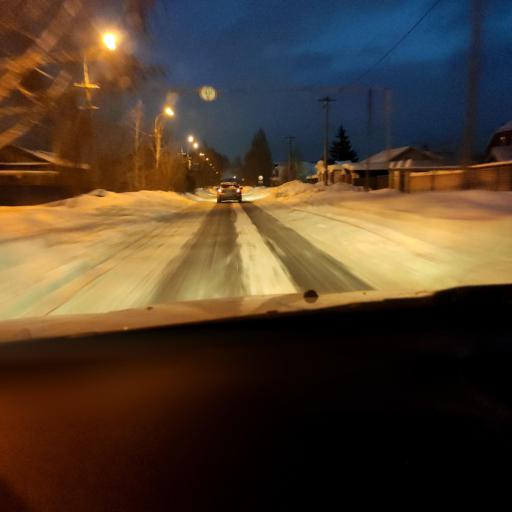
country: RU
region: Samara
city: Smyshlyayevka
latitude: 53.2404
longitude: 50.3331
